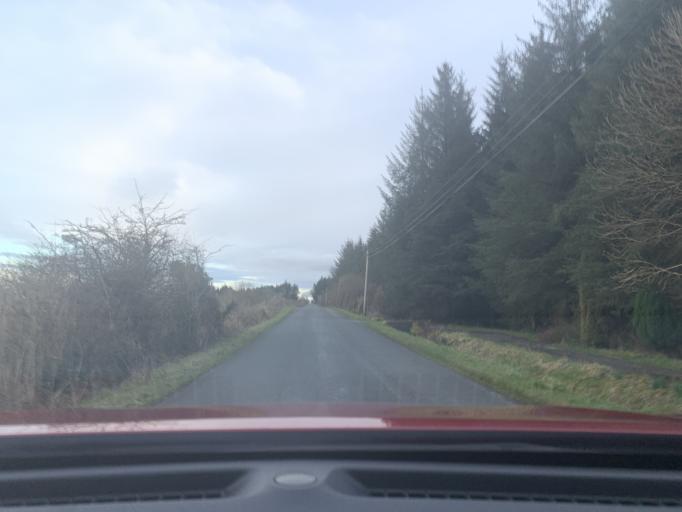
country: IE
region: Connaught
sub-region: Roscommon
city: Ballaghaderreen
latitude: 53.8848
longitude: -8.5674
